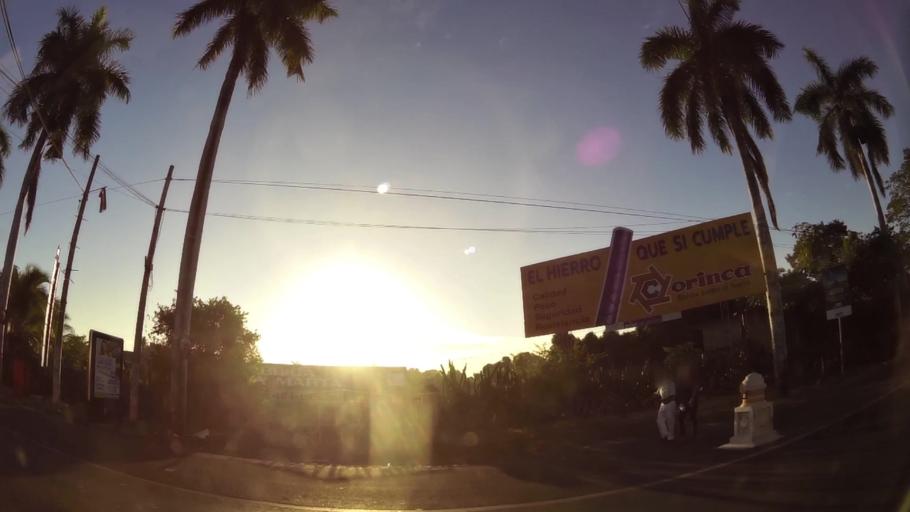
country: SV
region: Sonsonate
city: Sonsonate
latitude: 13.7225
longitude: -89.7191
